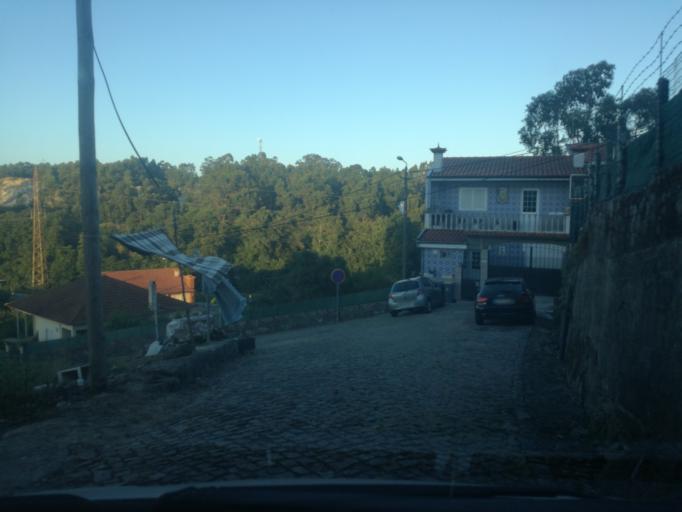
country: PT
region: Porto
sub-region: Maia
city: Nogueira
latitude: 41.2490
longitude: -8.6037
